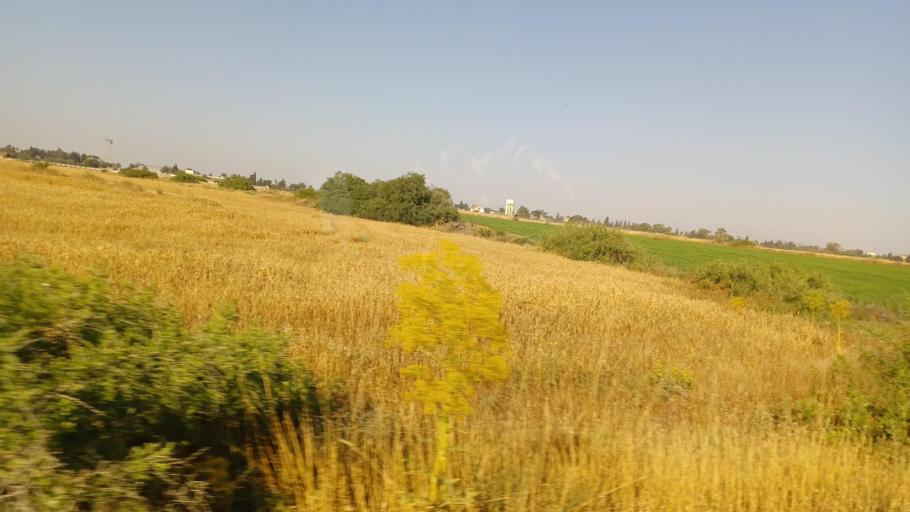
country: CY
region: Ammochostos
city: Acheritou
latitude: 35.0902
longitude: 33.9006
